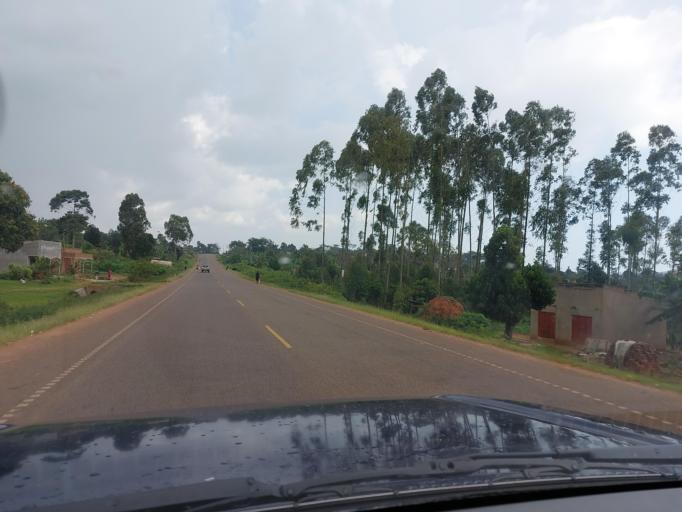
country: UG
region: Central Region
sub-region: Buikwe District
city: Buikwe
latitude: 0.2413
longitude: 32.9330
